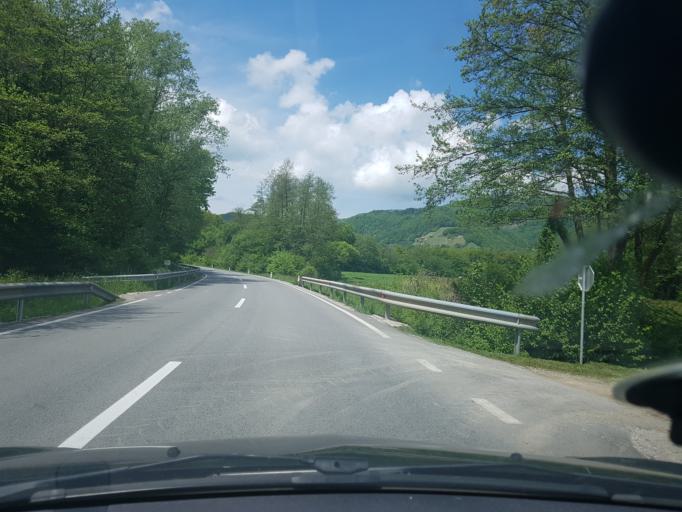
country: SI
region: Rogaska Slatina
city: Rogaska Slatina
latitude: 46.2459
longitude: 15.6520
